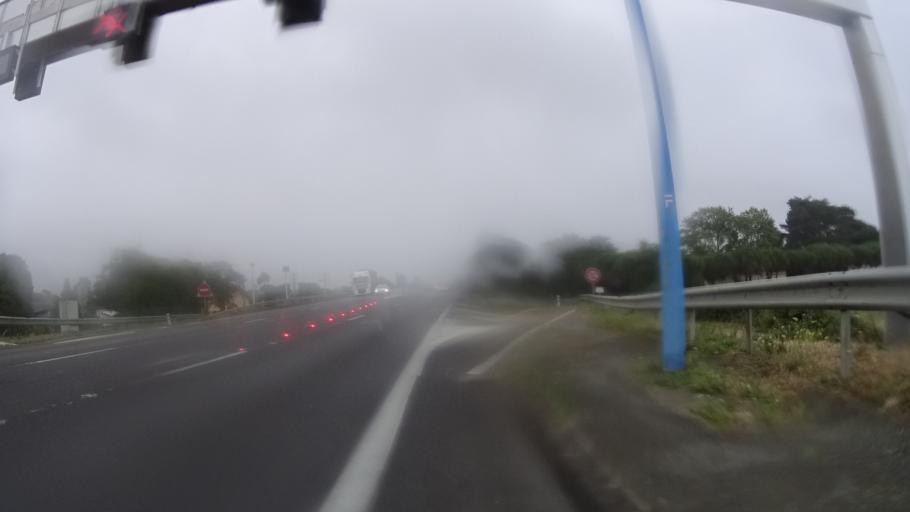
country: FR
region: Pays de la Loire
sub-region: Departement de la Loire-Atlantique
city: Saint-Brevin-les-Pins
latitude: 47.2688
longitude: -2.1621
